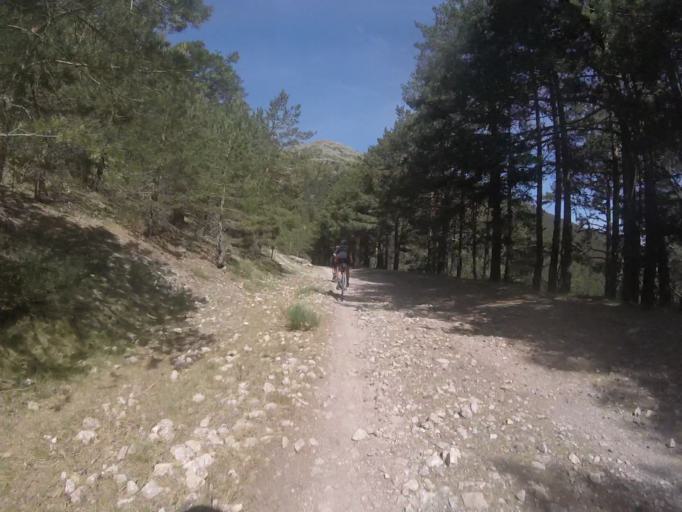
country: ES
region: Madrid
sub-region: Provincia de Madrid
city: Cercedilla
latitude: 40.7945
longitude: -4.0621
